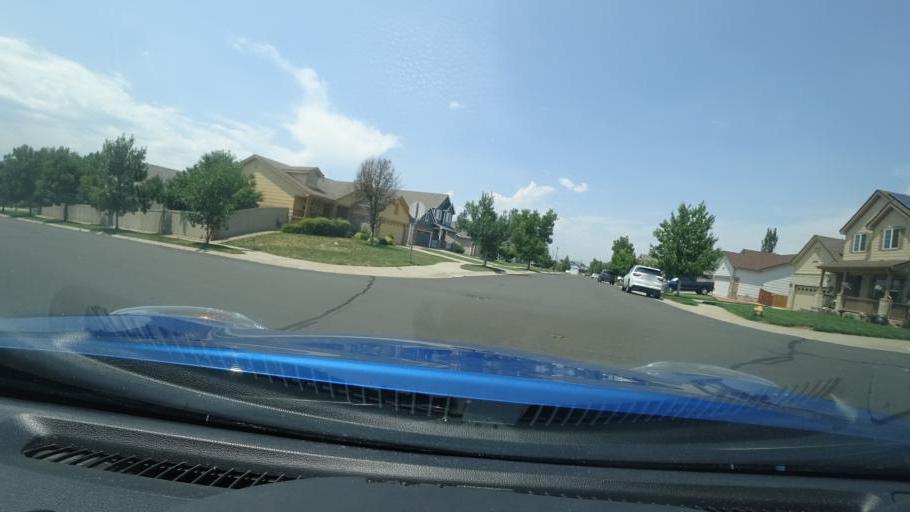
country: US
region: Colorado
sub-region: Adams County
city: Aurora
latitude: 39.6753
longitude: -104.7659
